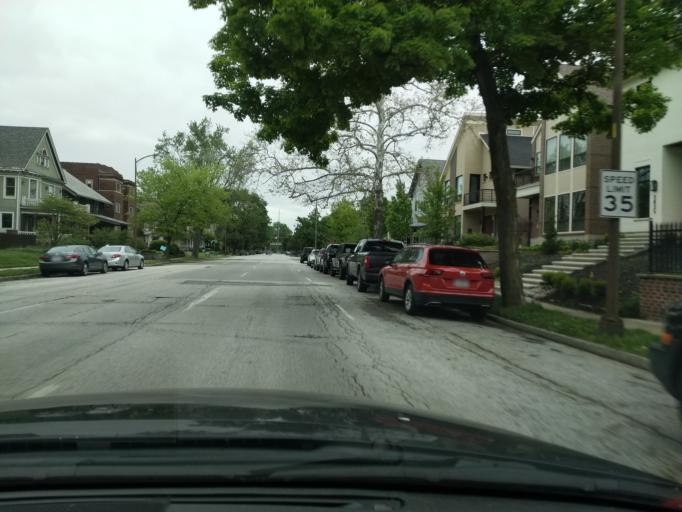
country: US
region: Indiana
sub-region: Marion County
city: Indianapolis
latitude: 39.7947
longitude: -86.1538
